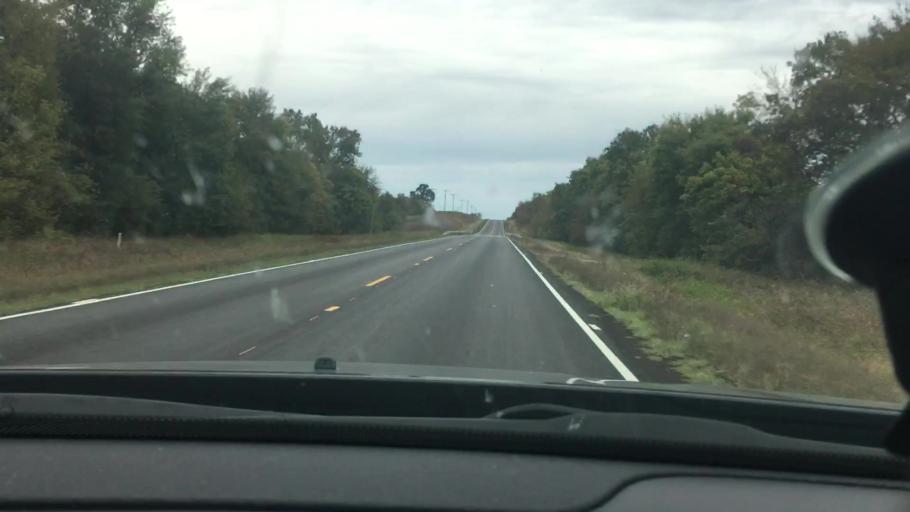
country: US
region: Oklahoma
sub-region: Coal County
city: Coalgate
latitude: 34.4051
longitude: -96.4245
